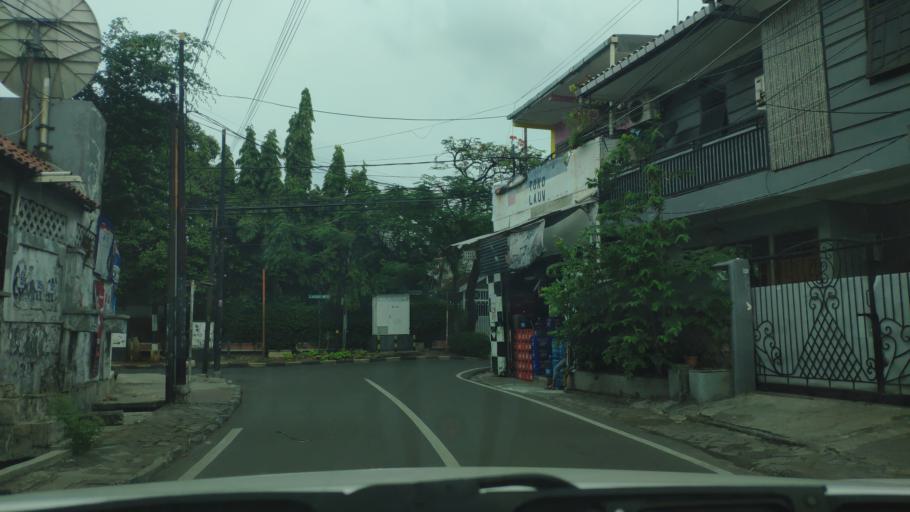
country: ID
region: Jakarta Raya
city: Jakarta
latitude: -6.1952
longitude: 106.7948
